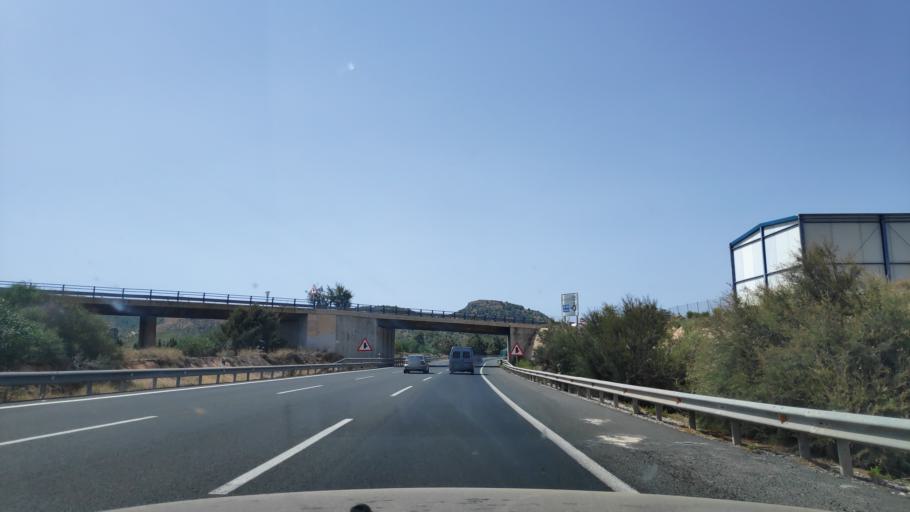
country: ES
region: Murcia
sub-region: Murcia
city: Murcia
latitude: 37.8851
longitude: -1.1377
